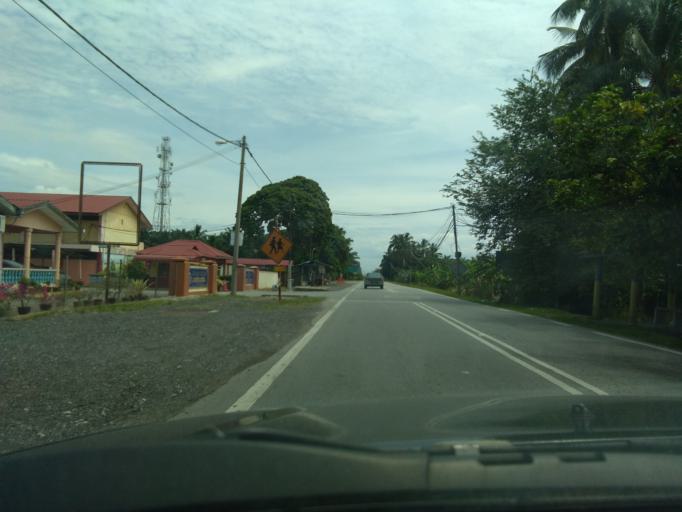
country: MY
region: Perak
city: Bagan Serai
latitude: 5.0555
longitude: 100.5928
